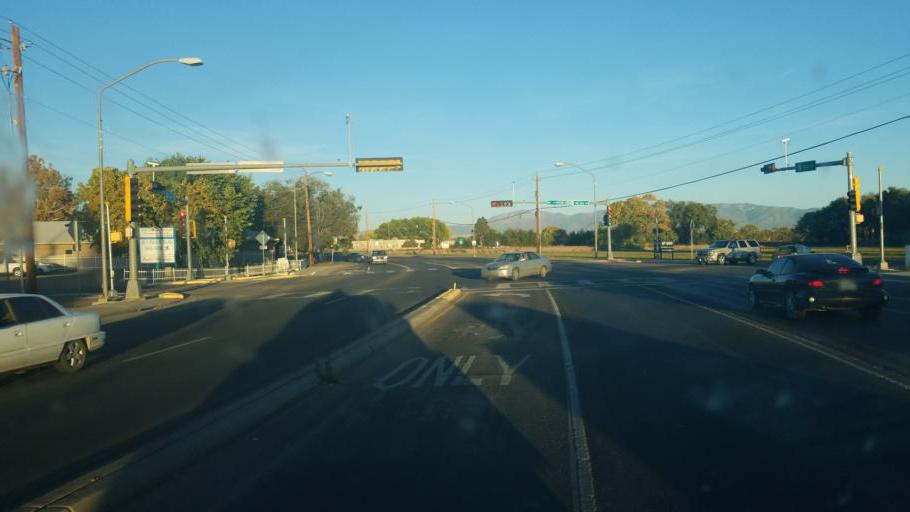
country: US
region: New Mexico
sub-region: Valencia County
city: Valencia
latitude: 34.8024
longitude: -106.7094
